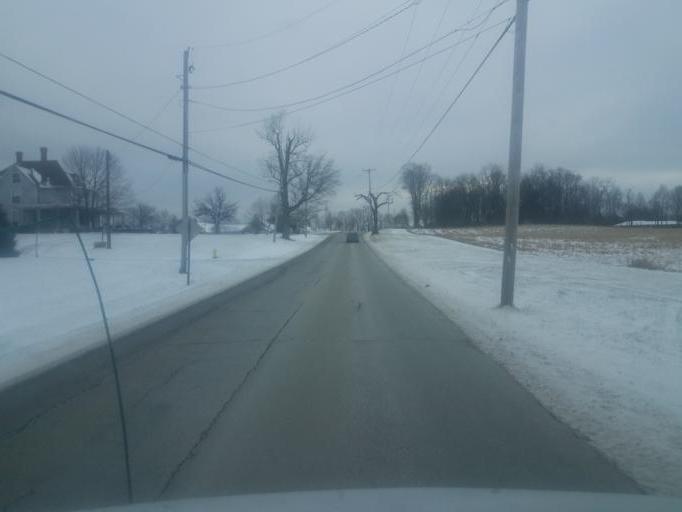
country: US
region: Ohio
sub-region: Richland County
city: Lexington
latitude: 40.7195
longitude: -82.5631
